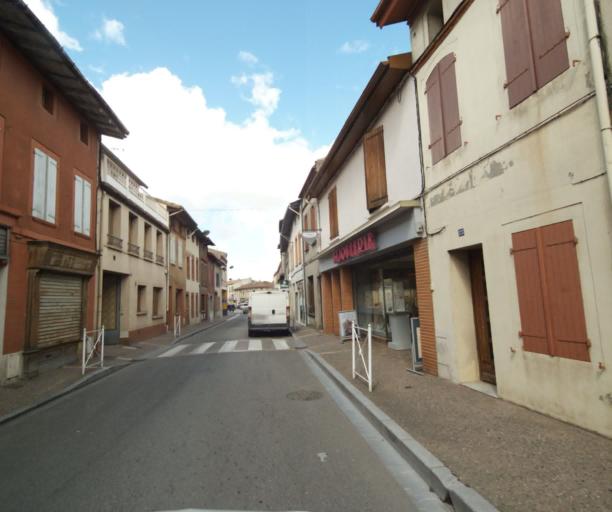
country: FR
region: Midi-Pyrenees
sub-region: Departement de l'Ariege
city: Saverdun
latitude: 43.2342
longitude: 1.5756
